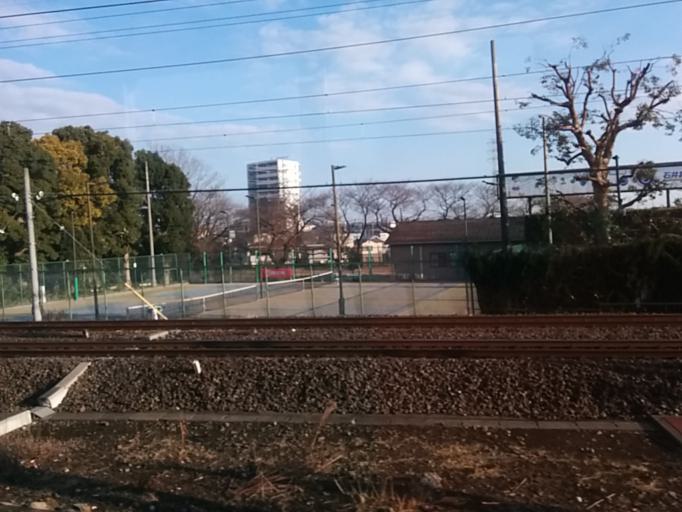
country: JP
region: Saitama
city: Asaka
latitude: 35.7919
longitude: 139.6043
